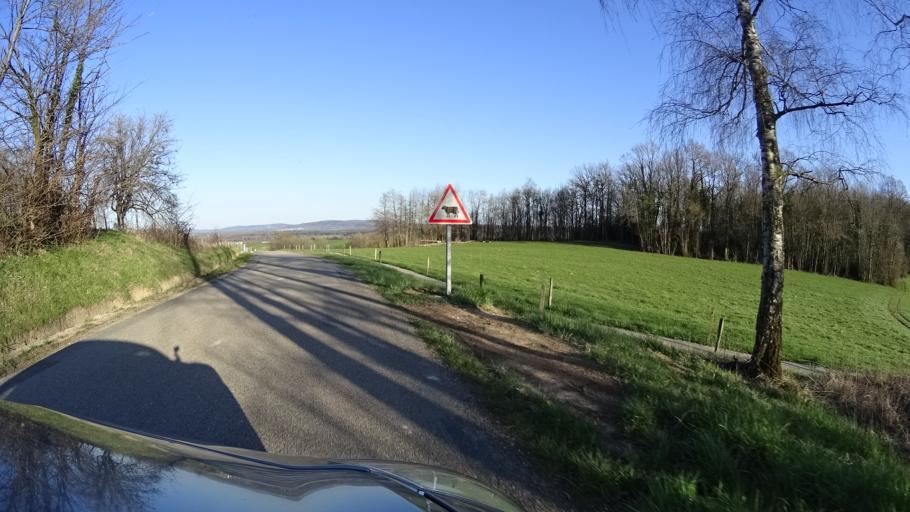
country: FR
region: Franche-Comte
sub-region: Departement du Doubs
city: Morre
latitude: 47.2061
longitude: 6.0532
